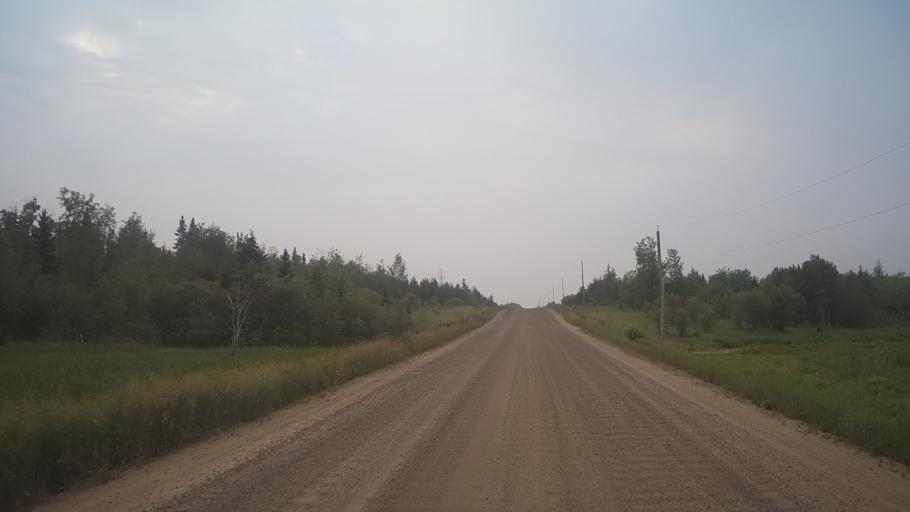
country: CA
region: Ontario
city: Hearst
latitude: 49.6324
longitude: -83.2783
